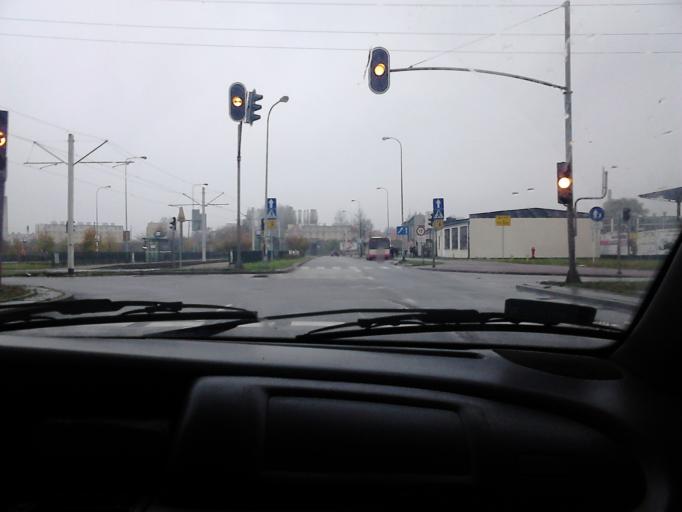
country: PL
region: Pomeranian Voivodeship
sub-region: Gdansk
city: Gdansk
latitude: 54.3601
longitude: 18.6916
